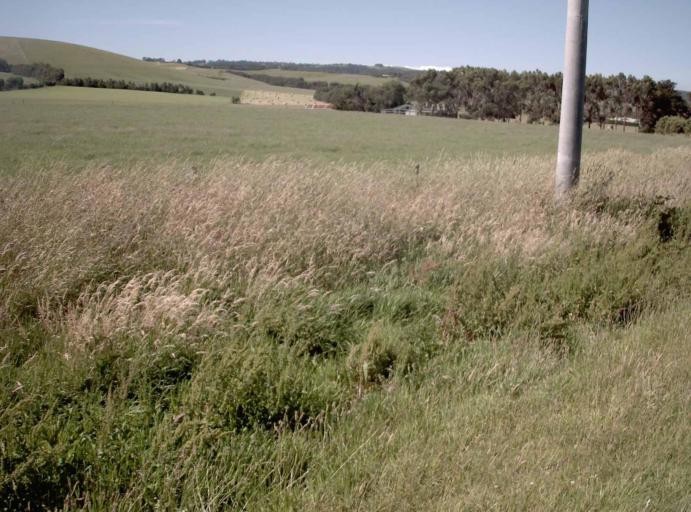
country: AU
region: Victoria
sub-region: Latrobe
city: Morwell
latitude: -38.6624
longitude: 146.4499
